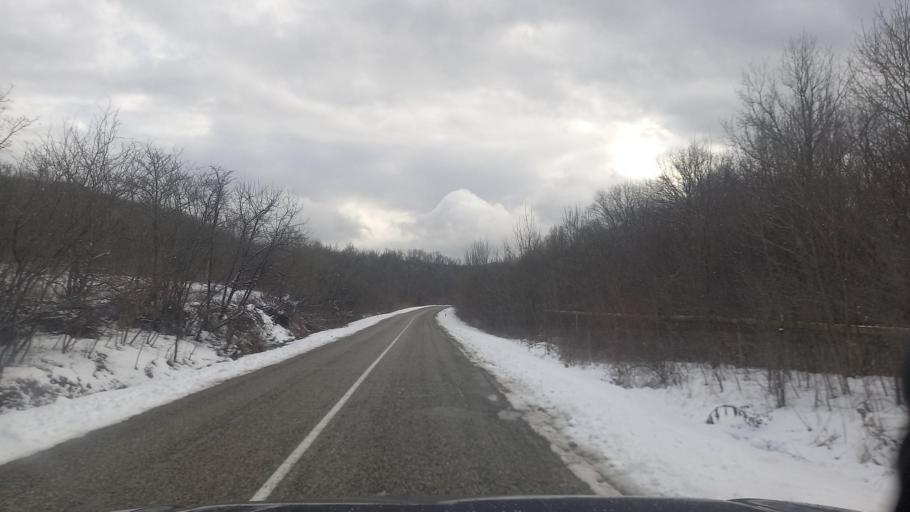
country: RU
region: Krasnodarskiy
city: Smolenskaya
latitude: 44.7388
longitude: 38.8376
